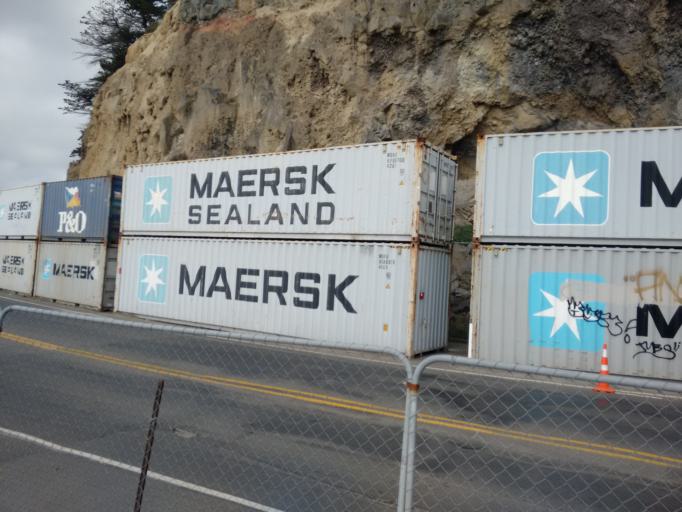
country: NZ
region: Canterbury
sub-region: Christchurch City
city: Christchurch
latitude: -43.5646
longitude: 172.7539
